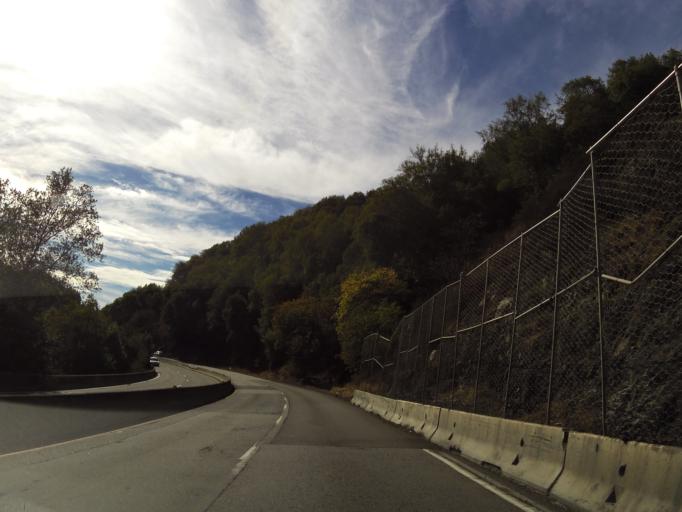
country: US
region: California
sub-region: Santa Clara County
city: Los Gatos
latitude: 37.2112
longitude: -121.9898
